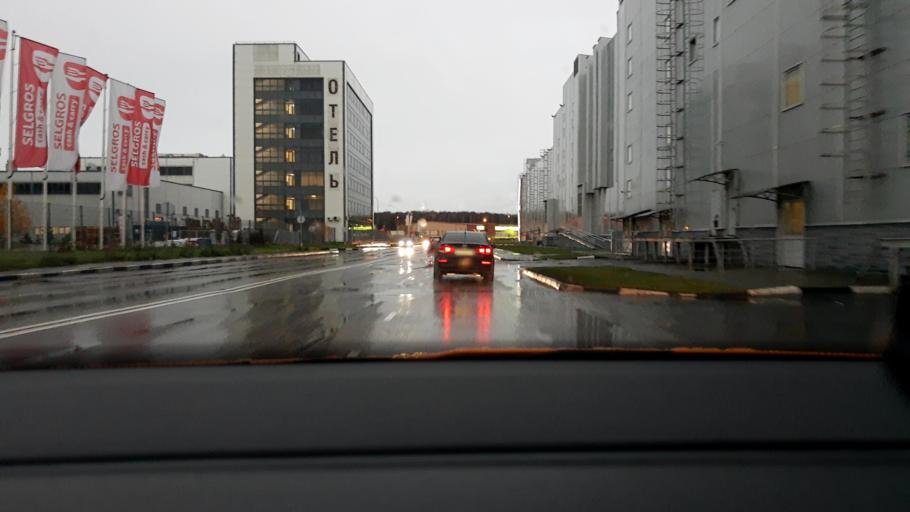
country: RU
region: Moscow
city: Lianozovo
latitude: 55.9138
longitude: 37.5851
